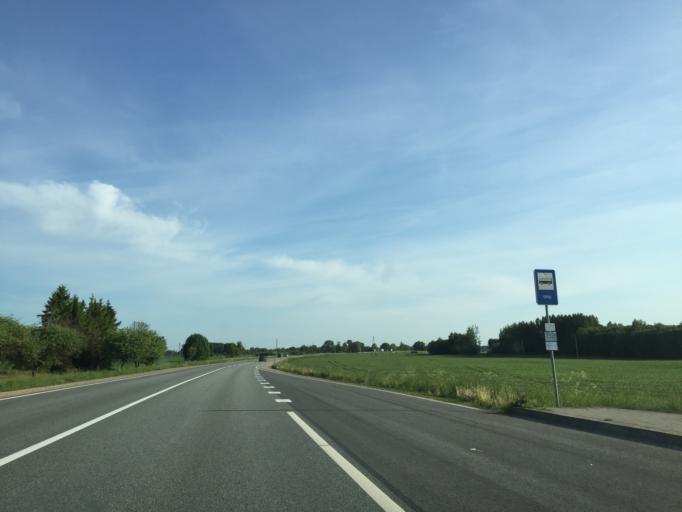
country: LV
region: Bauskas Rajons
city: Bauska
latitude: 56.4858
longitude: 24.1773
